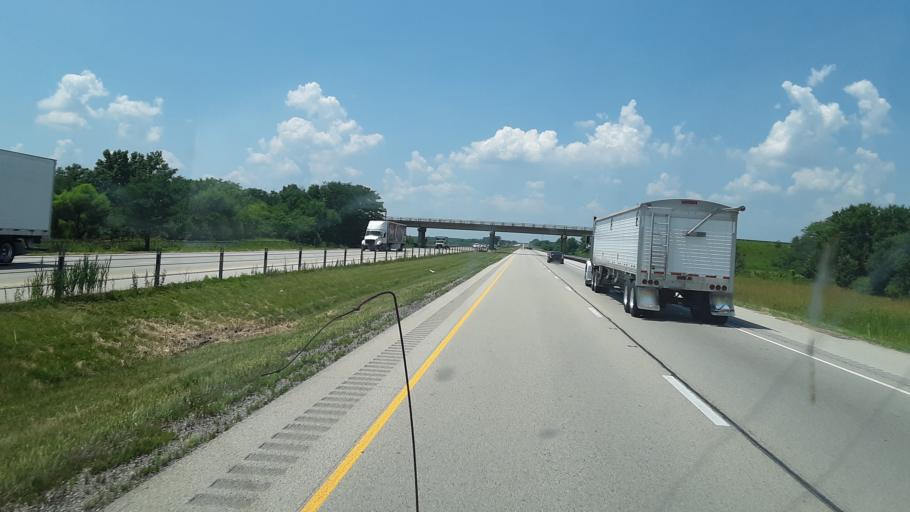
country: US
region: Illinois
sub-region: LaSalle County
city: Marseilles
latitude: 41.3758
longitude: -88.6493
